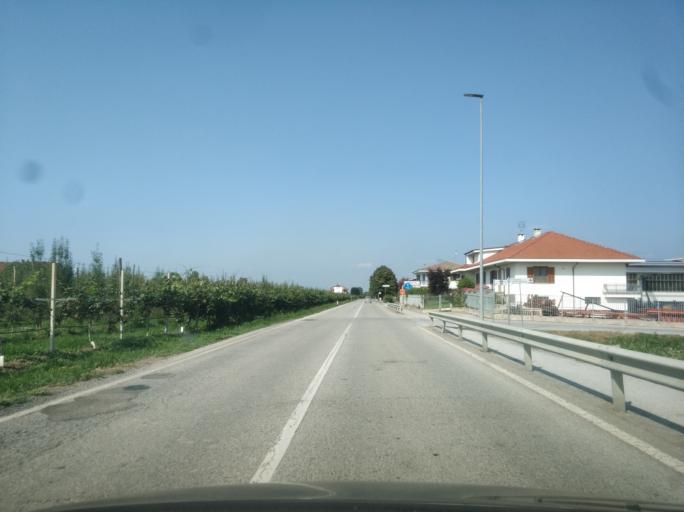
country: IT
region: Piedmont
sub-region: Provincia di Cuneo
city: Centallo
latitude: 44.5076
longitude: 7.5887
